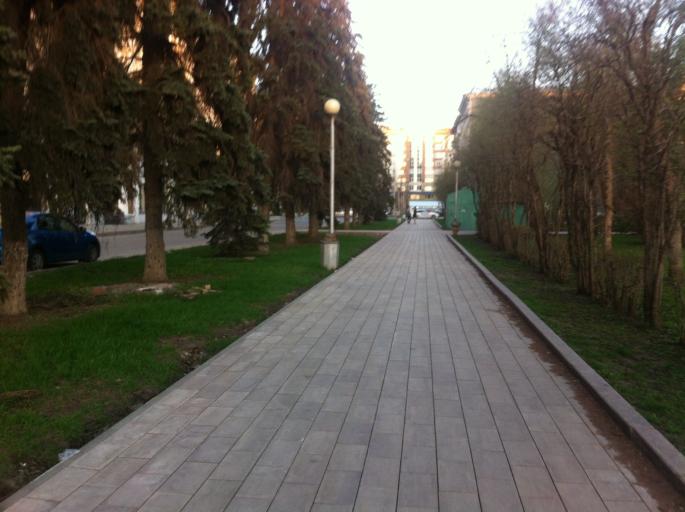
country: RU
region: Samara
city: Samara
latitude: 53.2017
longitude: 50.1134
